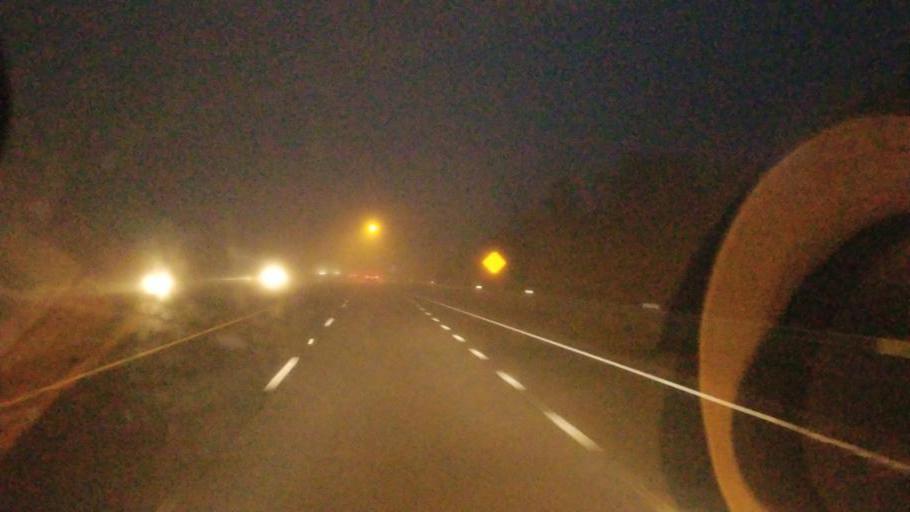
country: US
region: Ohio
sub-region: Ross County
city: Chillicothe
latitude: 39.3832
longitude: -82.9694
